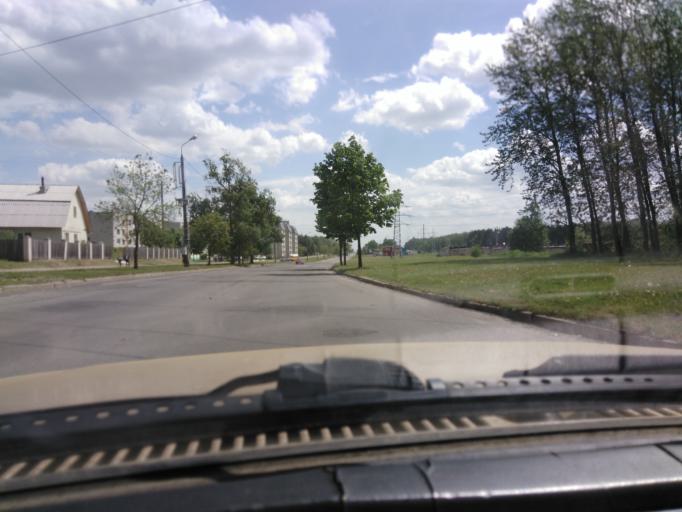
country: BY
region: Mogilev
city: Mahilyow
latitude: 53.9497
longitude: 30.3453
